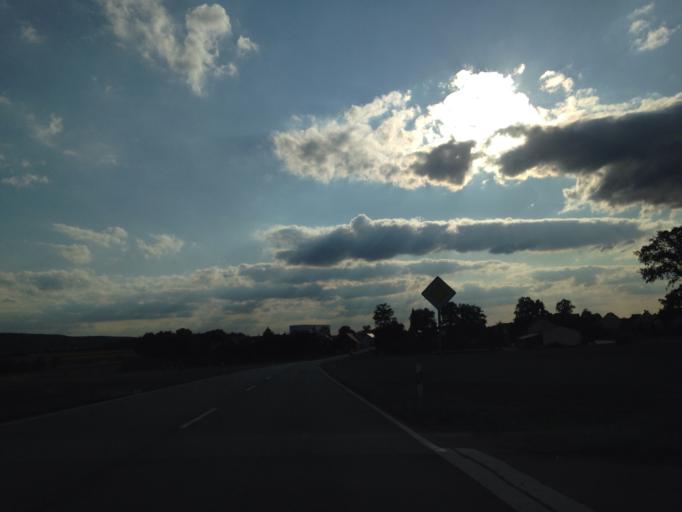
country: DE
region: Bavaria
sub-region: Upper Palatinate
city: Freystadt
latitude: 49.1649
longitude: 11.2790
